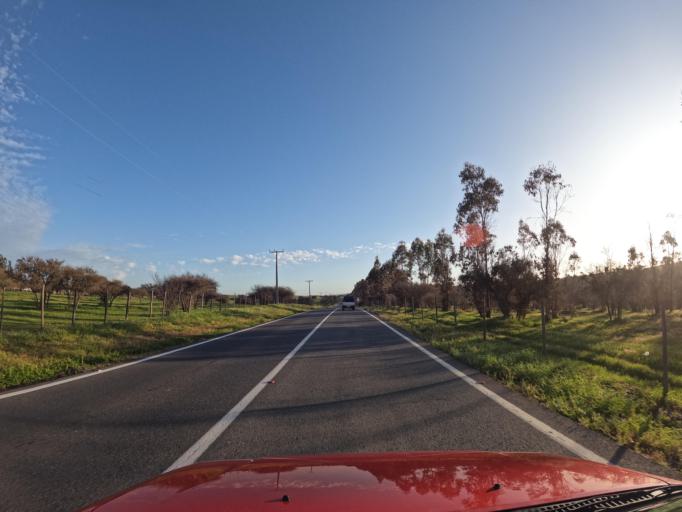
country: CL
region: O'Higgins
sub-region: Provincia de Colchagua
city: Santa Cruz
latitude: -34.2277
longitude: -71.7252
